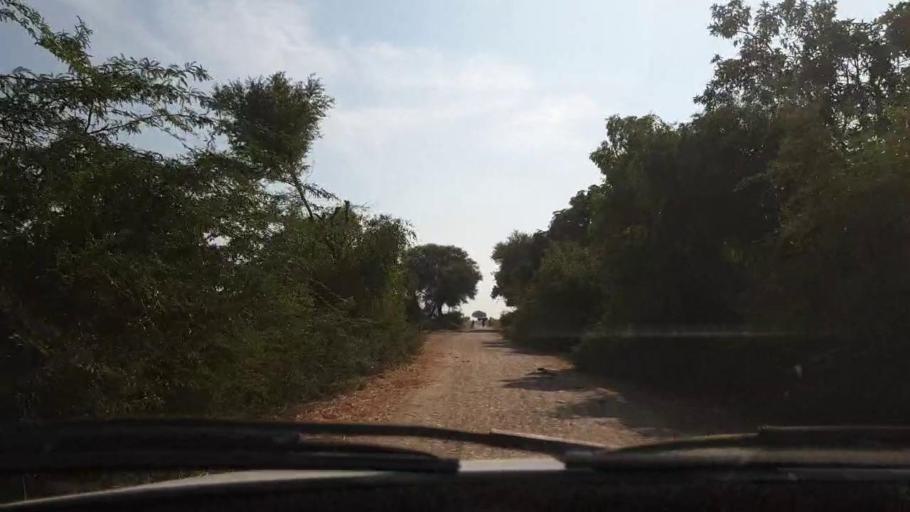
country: PK
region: Sindh
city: Bulri
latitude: 24.9571
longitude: 68.4446
